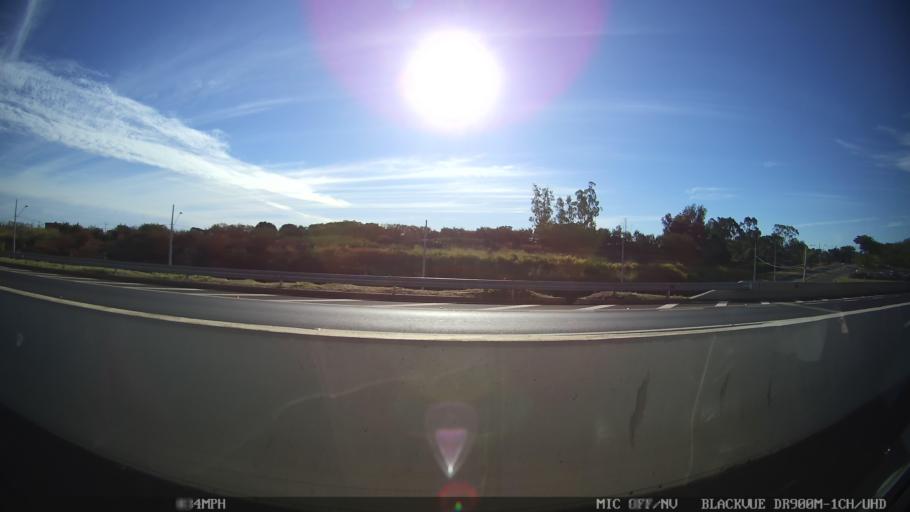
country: BR
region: Sao Paulo
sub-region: Sao Jose Do Rio Preto
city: Sao Jose do Rio Preto
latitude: -20.8558
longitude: -49.4051
